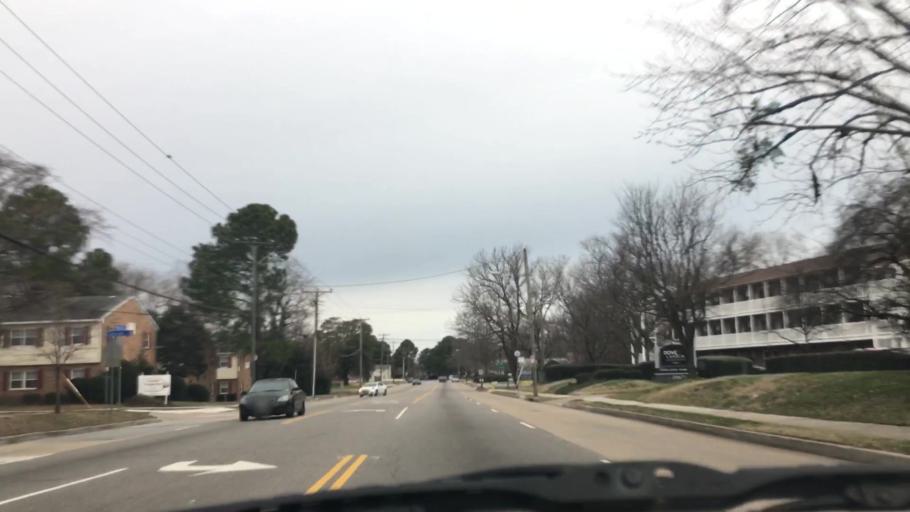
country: US
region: Virginia
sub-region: City of Norfolk
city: Norfolk
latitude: 36.8784
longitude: -76.2333
